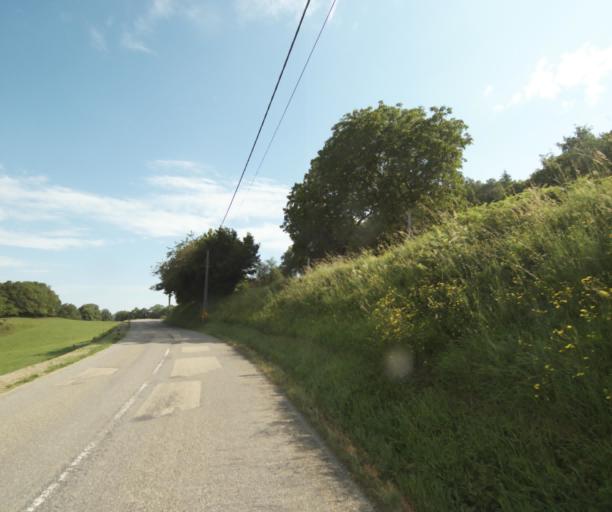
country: FR
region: Rhone-Alpes
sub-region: Departement de la Haute-Savoie
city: Lyaud
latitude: 46.3285
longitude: 6.5086
